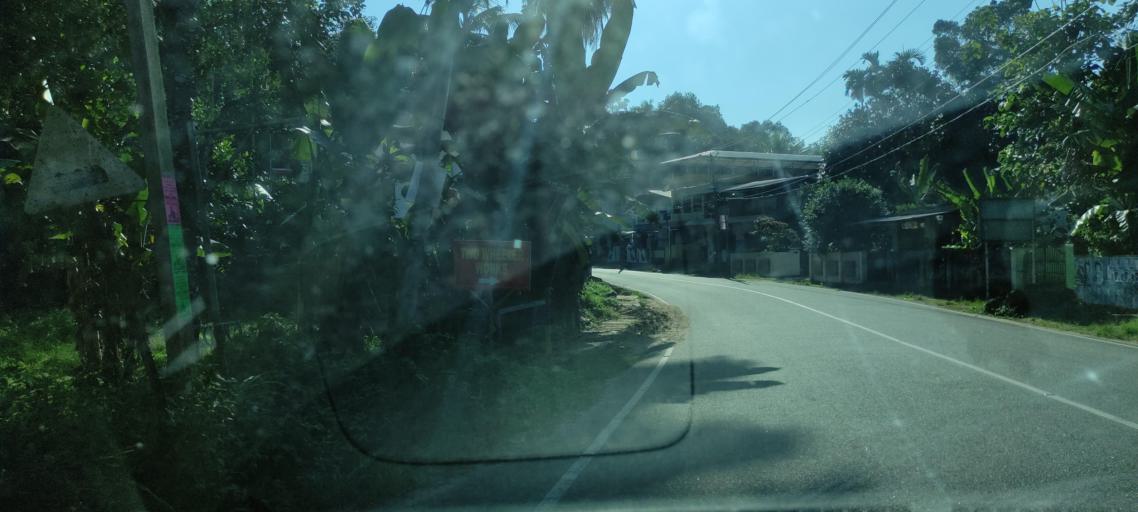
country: IN
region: Kerala
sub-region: Pattanamtitta
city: Pathanamthitta
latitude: 9.2259
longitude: 76.7534
